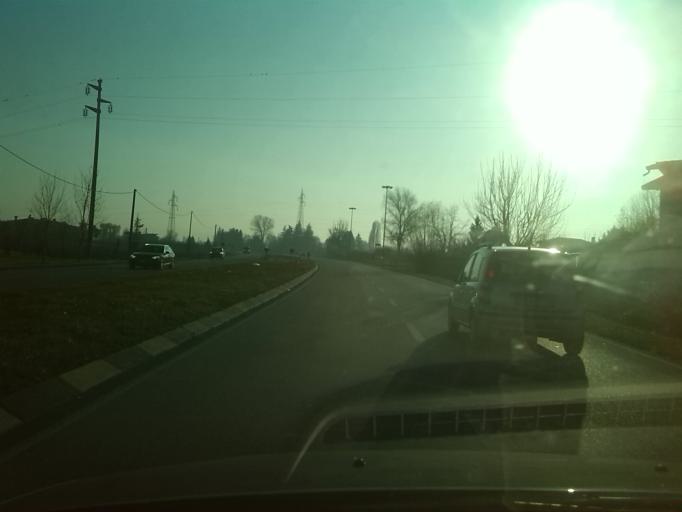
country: IT
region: Friuli Venezia Giulia
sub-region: Provincia di Udine
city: Latisana
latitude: 45.7839
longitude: 13.0217
